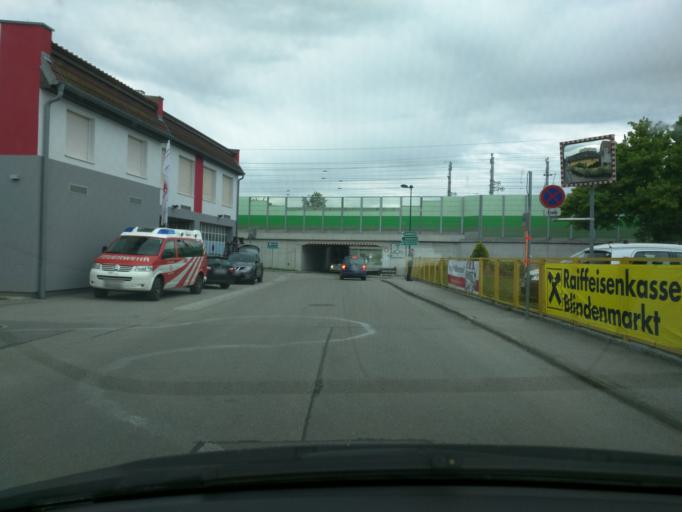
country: AT
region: Lower Austria
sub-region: Politischer Bezirk Melk
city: Blindenmarkt
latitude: 48.1261
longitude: 14.9872
